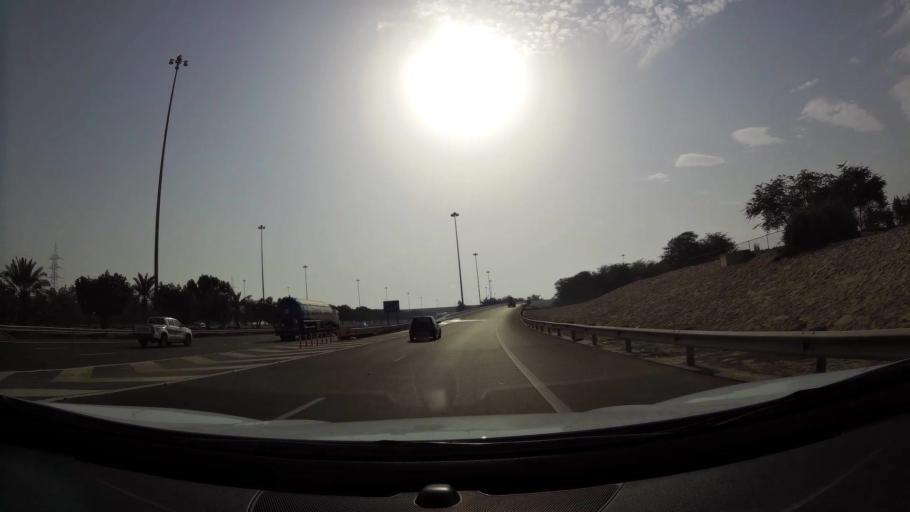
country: AE
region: Abu Dhabi
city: Abu Dhabi
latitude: 24.2528
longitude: 54.7051
